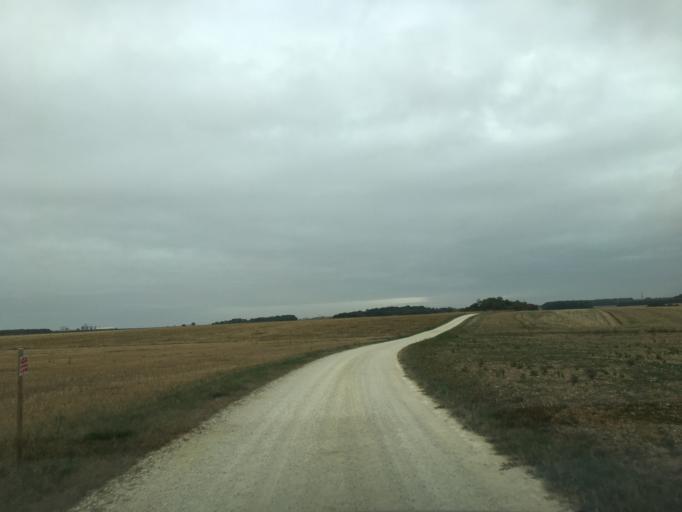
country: FR
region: Poitou-Charentes
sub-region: Departement des Deux-Sevres
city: Beauvoir-sur-Niort
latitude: 46.0819
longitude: -0.4930
